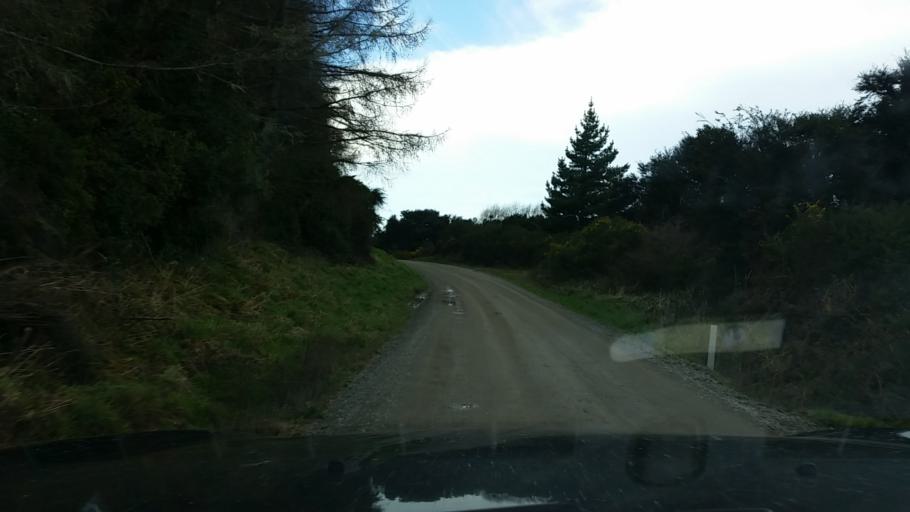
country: NZ
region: Nelson
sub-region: Nelson City
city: Nelson
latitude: -41.5772
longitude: 173.4362
